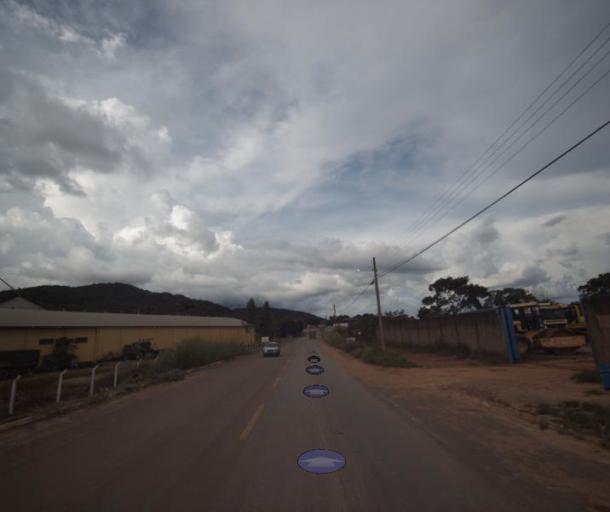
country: BR
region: Goias
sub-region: Niquelandia
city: Niquelandia
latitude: -14.4692
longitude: -48.4851
